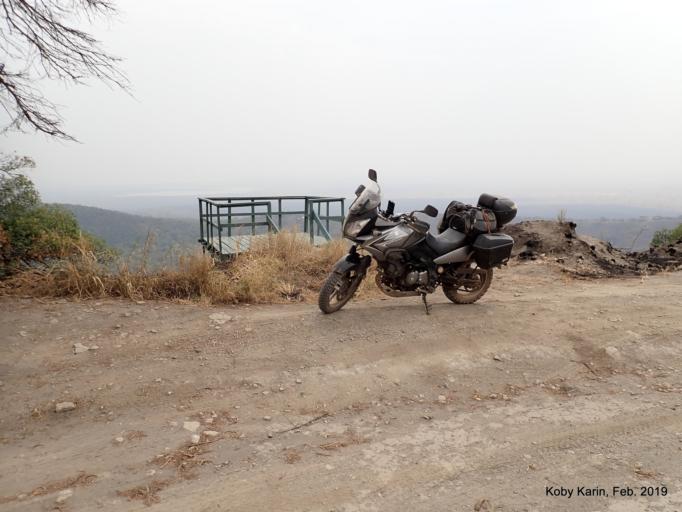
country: UG
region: Western Region
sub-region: Kasese District
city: Kilembe
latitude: -0.0340
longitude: 29.9746
